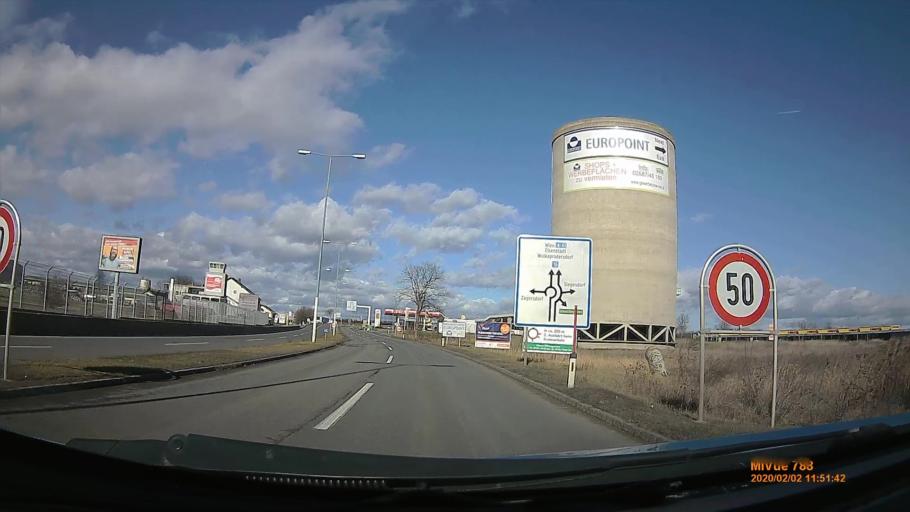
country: AT
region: Burgenland
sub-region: Eisenstadt-Umgebung
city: Zagersdorf
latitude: 47.7716
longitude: 16.5297
